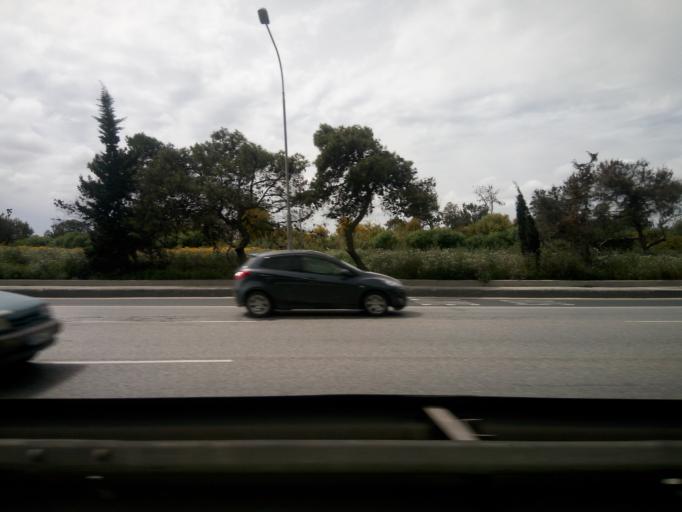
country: MT
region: Paola
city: Paola
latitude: 35.8751
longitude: 14.4955
